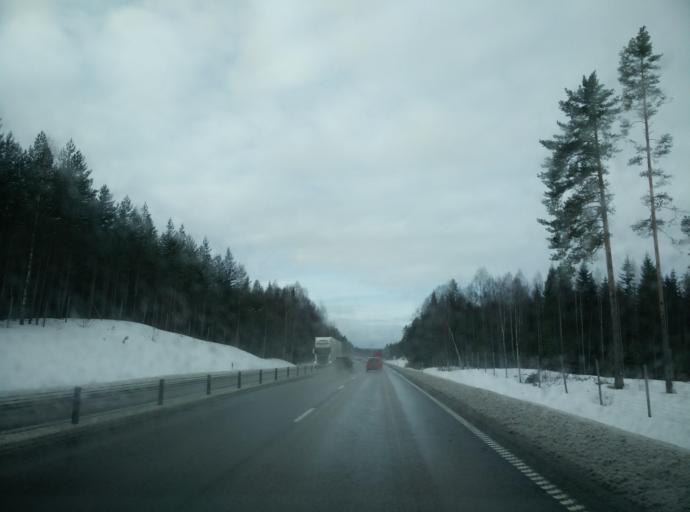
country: SE
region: Dalarna
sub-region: Hedemora Kommun
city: Langshyttan
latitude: 60.5566
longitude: 16.0571
